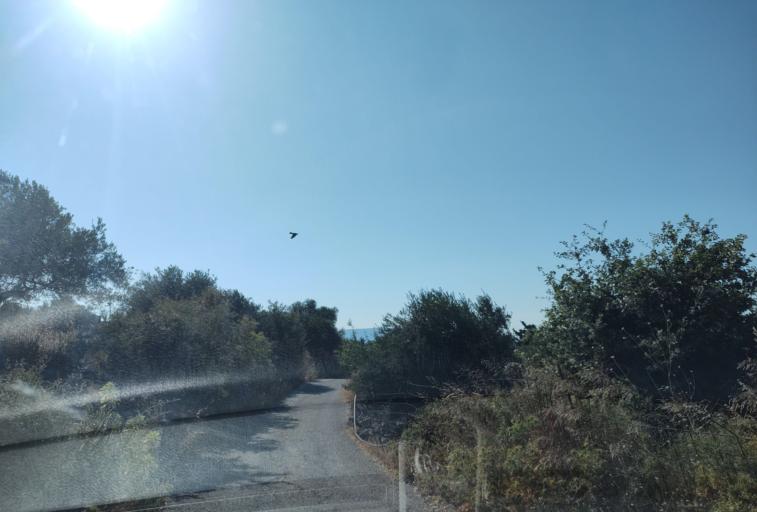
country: GR
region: Crete
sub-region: Nomos Chanias
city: Georgioupolis
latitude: 35.3963
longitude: 24.2365
